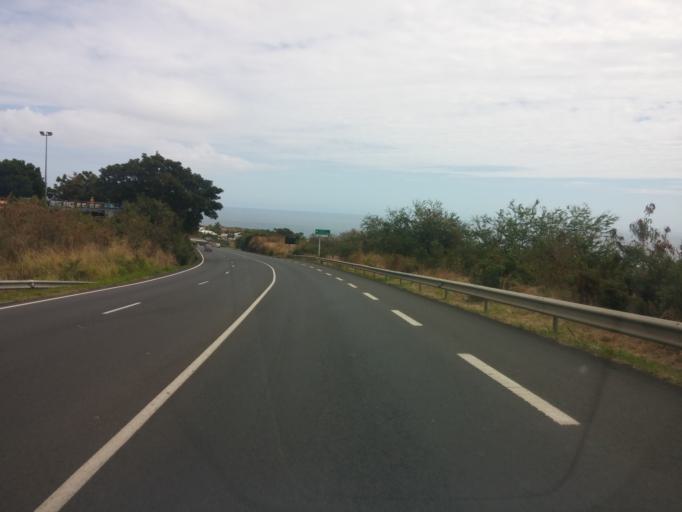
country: RE
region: Reunion
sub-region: Reunion
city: Saint-Paul
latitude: -21.0192
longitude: 55.2695
